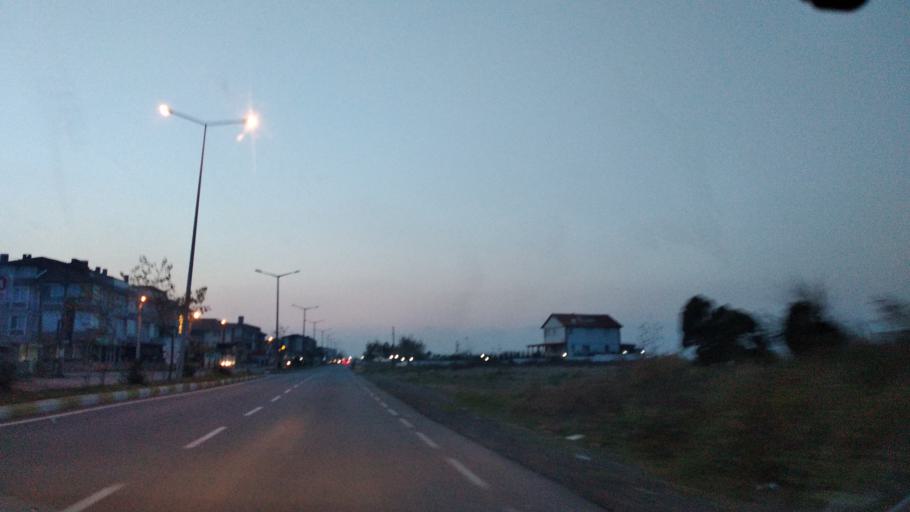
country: TR
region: Sakarya
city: Karasu
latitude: 41.0981
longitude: 30.7253
